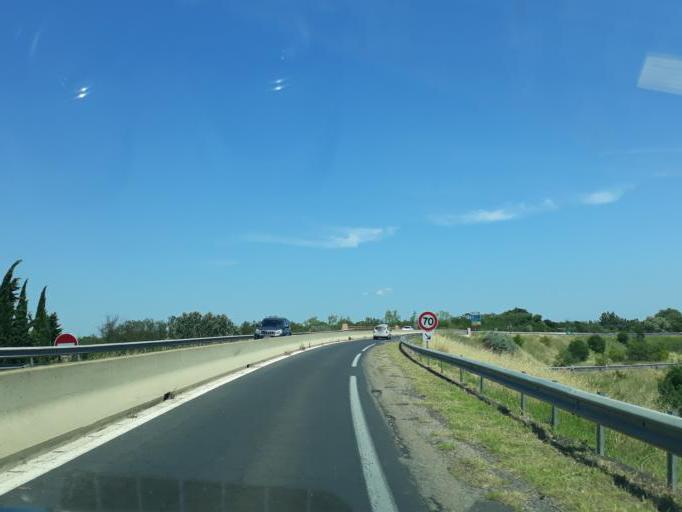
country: FR
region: Languedoc-Roussillon
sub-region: Departement de l'Herault
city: Vias
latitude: 43.3090
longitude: 3.4296
